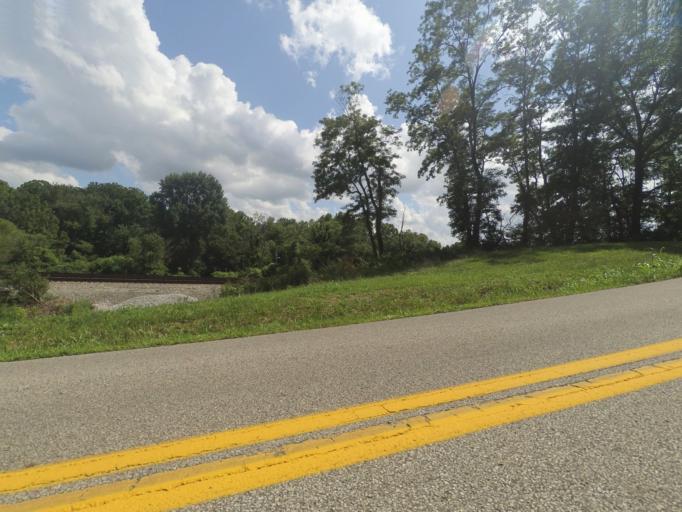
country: US
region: West Virginia
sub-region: Cabell County
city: Pea Ridge
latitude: 38.4276
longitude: -82.3233
